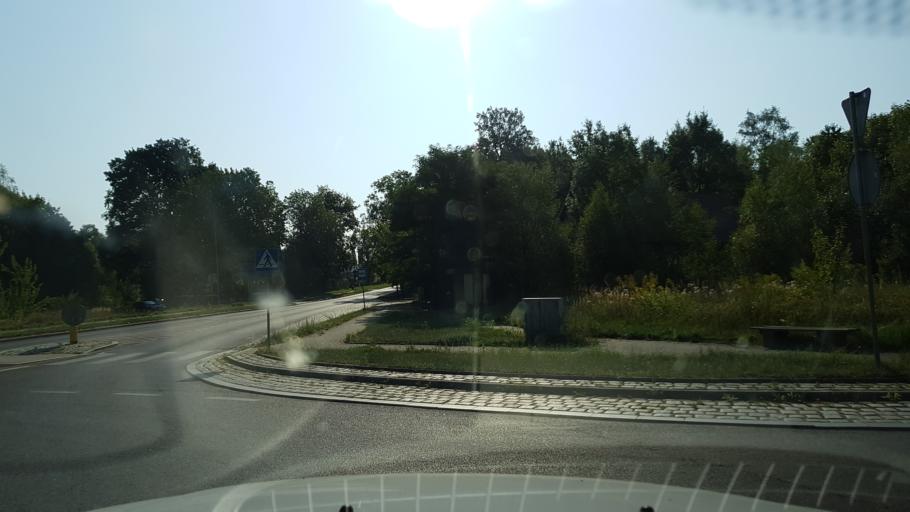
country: PL
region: West Pomeranian Voivodeship
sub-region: Powiat gryficki
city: Ploty
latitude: 53.7995
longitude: 15.2686
